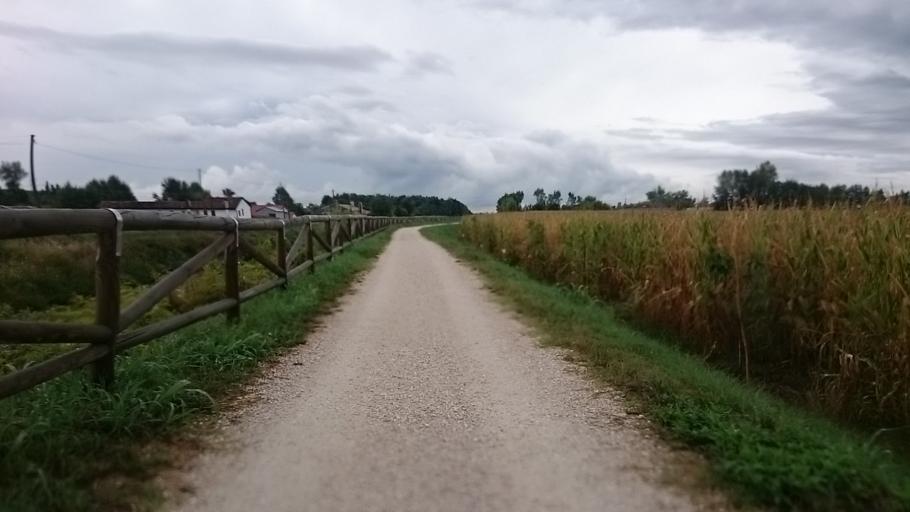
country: IT
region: Veneto
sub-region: Provincia di Padova
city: Loreggiola
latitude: 45.6264
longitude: 11.9260
